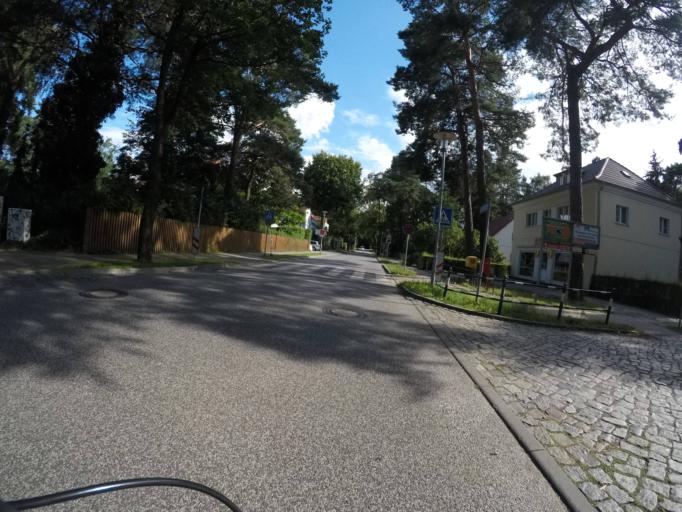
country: DE
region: Brandenburg
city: Michendorf
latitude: 52.3303
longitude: 13.0561
